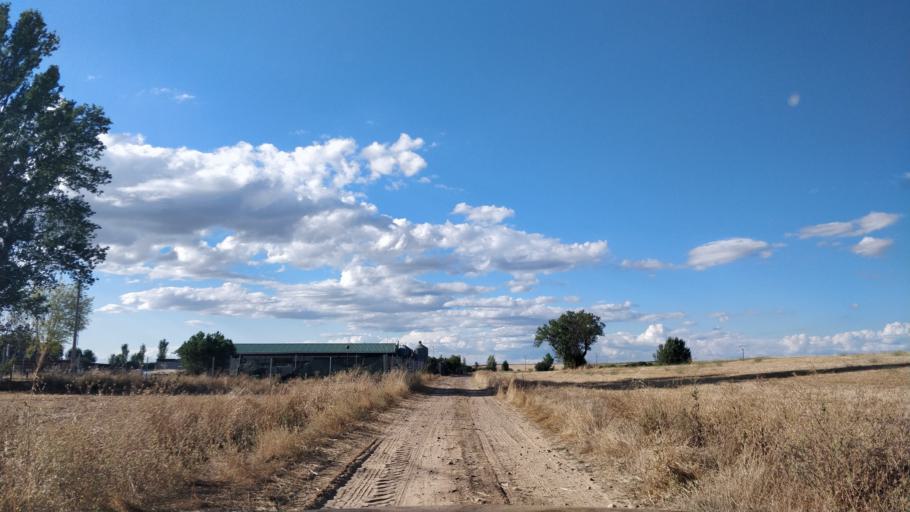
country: ES
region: Castille and Leon
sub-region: Provincia de Leon
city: Valverde-Enrique
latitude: 42.3281
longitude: -5.2794
